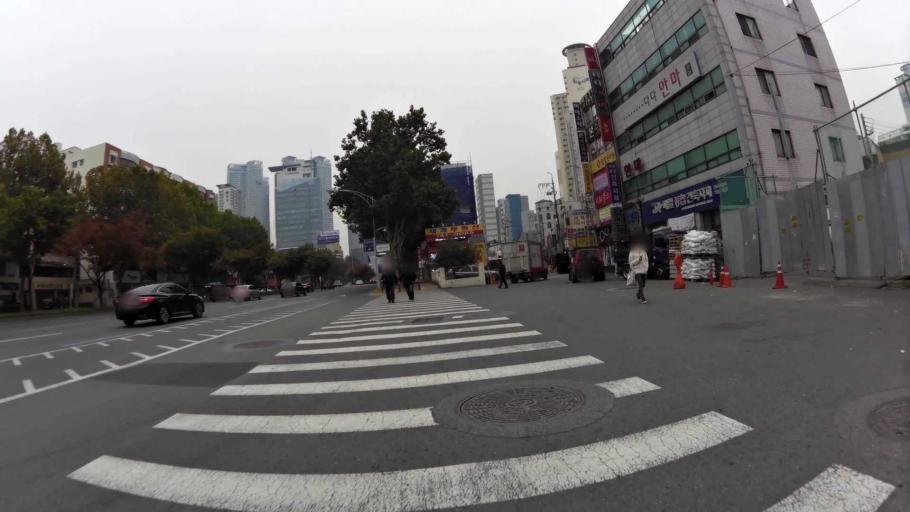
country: KR
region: Daegu
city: Daegu
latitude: 35.8593
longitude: 128.6209
